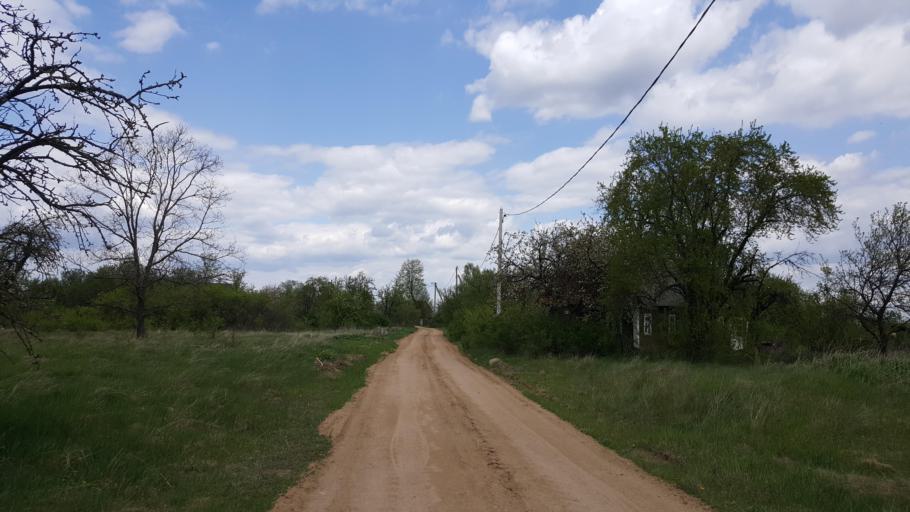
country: BY
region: Brest
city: Zhabinka
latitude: 52.3907
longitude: 24.0984
